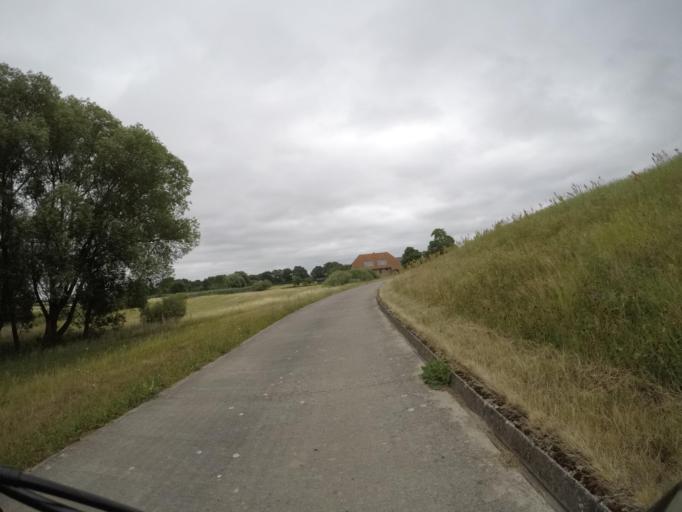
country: DE
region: Lower Saxony
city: Hitzacker
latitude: 53.1592
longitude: 11.0678
